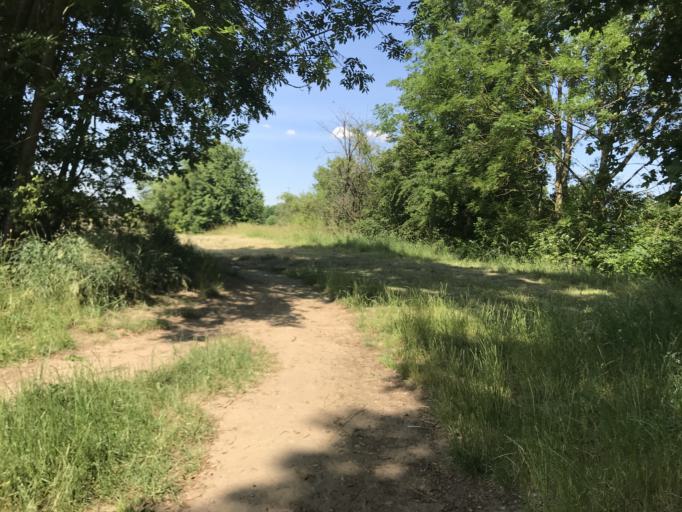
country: DE
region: Hesse
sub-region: Regierungsbezirk Darmstadt
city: Frankfurt am Main
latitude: 50.1694
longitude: 8.6512
